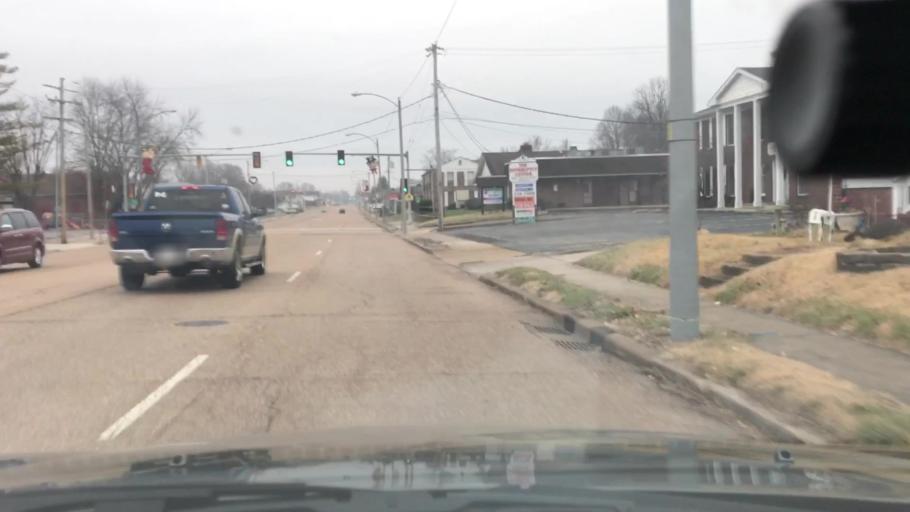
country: US
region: Illinois
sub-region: Saint Clair County
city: Swansea
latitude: 38.5465
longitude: -90.0325
